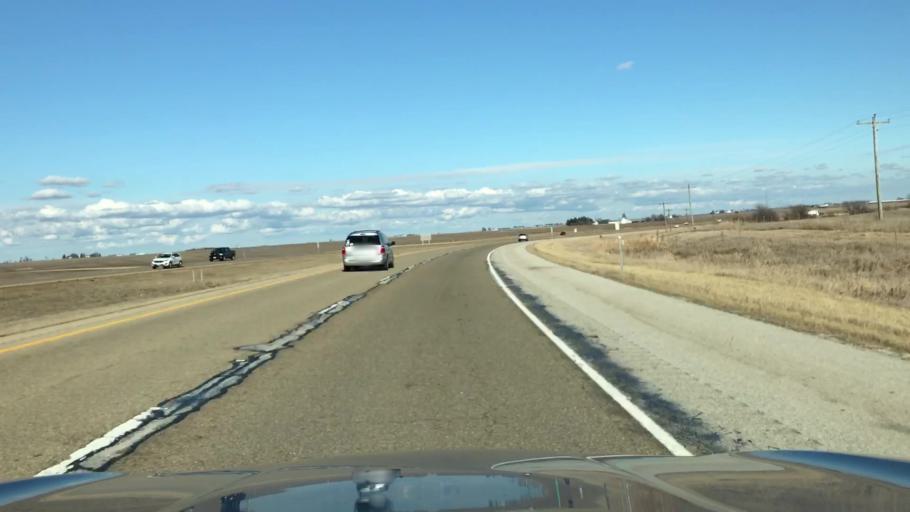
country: US
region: Illinois
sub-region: McLean County
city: Lexington
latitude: 40.6521
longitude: -88.8054
